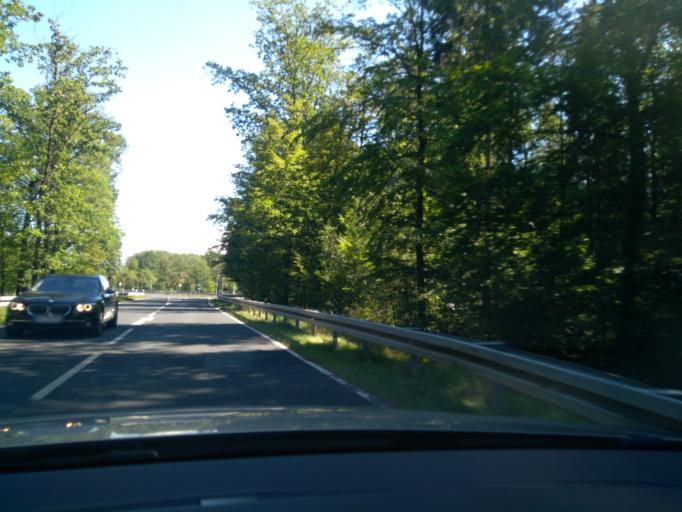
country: DE
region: Saxony
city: Grossrohrsdorf
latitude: 51.1358
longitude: 13.9868
